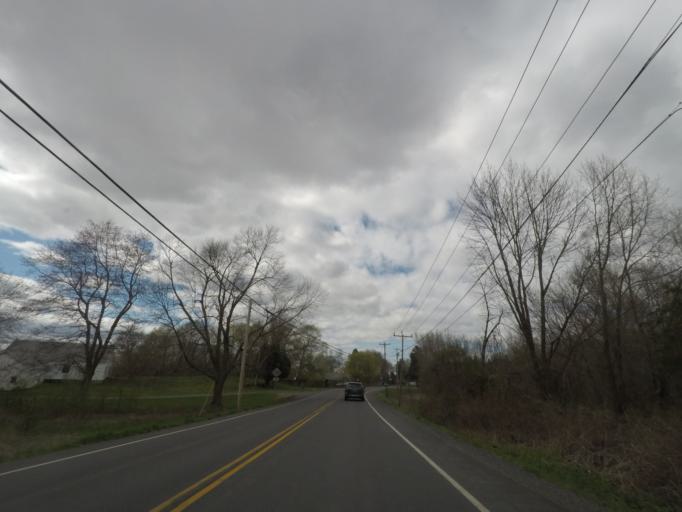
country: US
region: New York
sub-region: Columbia County
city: Chatham
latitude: 42.3607
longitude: -73.6130
